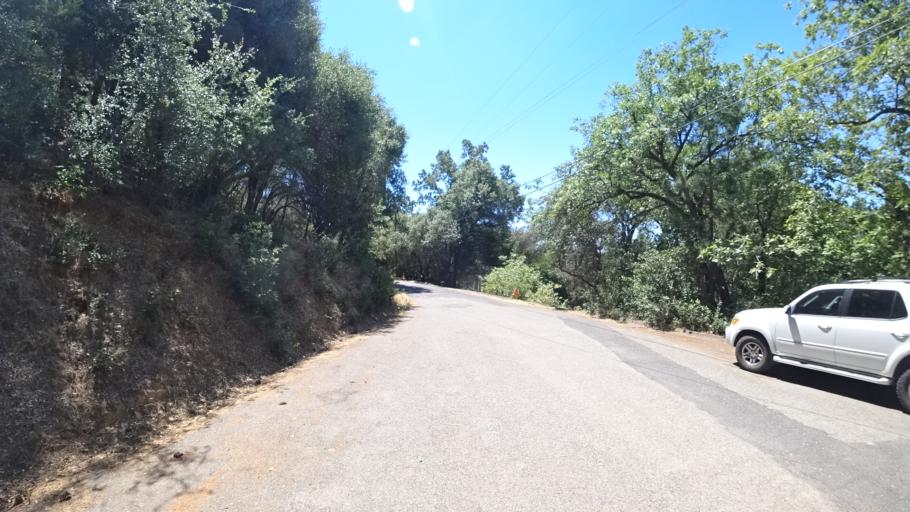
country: US
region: California
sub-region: Calaveras County
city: Murphys
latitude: 38.1370
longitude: -120.4505
